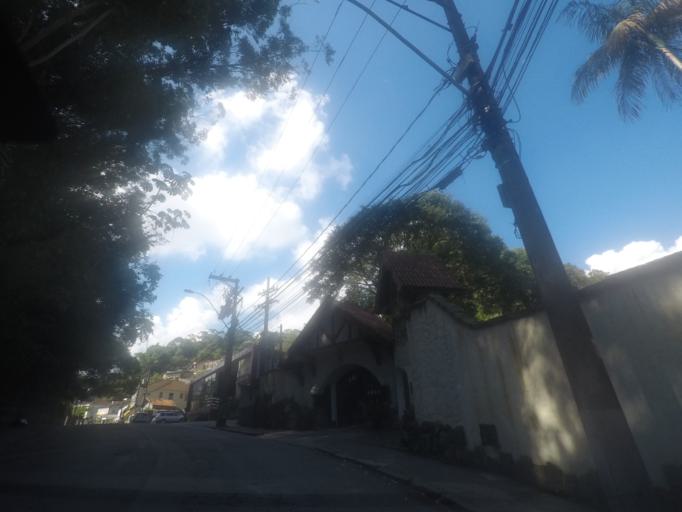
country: BR
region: Rio de Janeiro
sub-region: Petropolis
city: Petropolis
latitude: -22.5203
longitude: -43.1904
